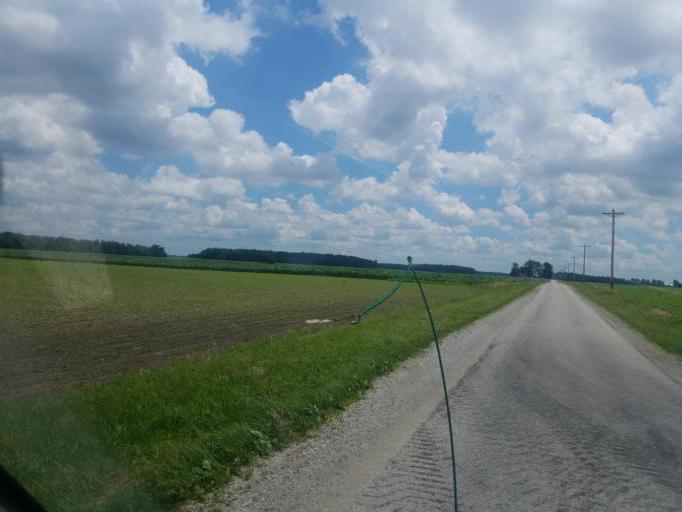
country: US
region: Ohio
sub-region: Huron County
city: Willard
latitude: 41.0298
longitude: -82.8306
